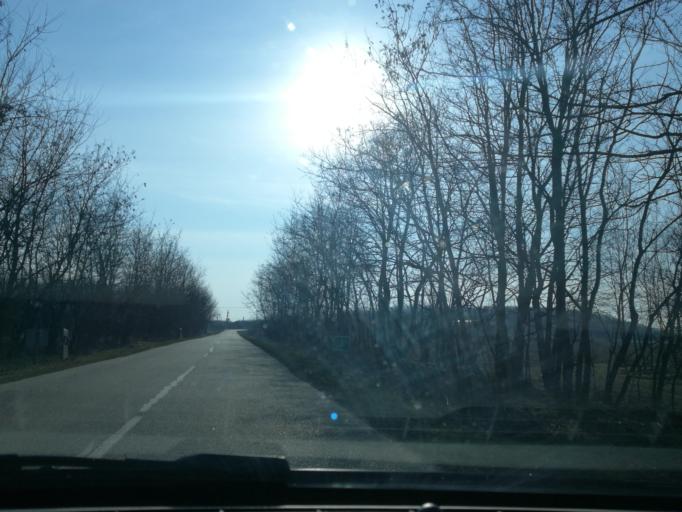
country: HU
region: Szabolcs-Szatmar-Bereg
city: Demecser
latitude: 48.0494
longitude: 21.9679
